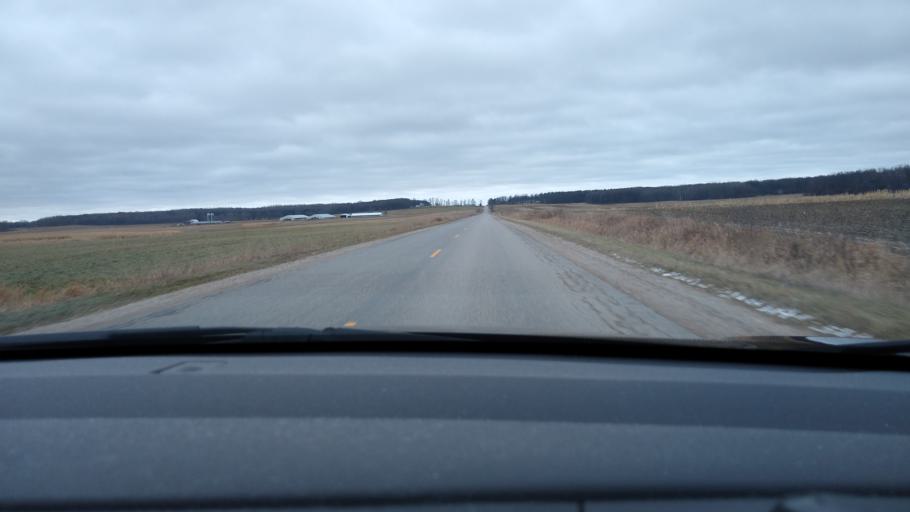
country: US
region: Michigan
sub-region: Missaukee County
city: Lake City
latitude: 44.3093
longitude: -85.0545
